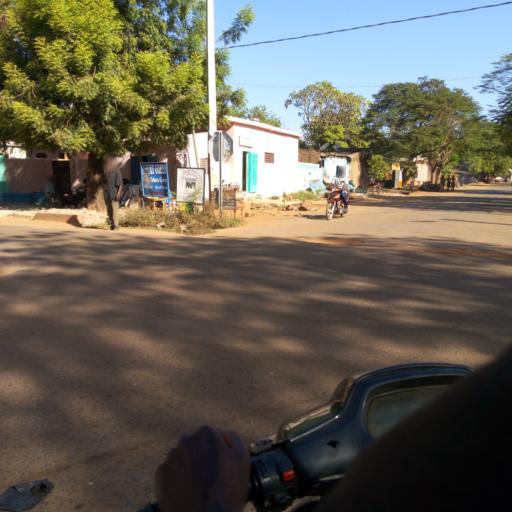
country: ML
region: Bamako
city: Bamako
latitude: 12.6550
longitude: -8.0158
